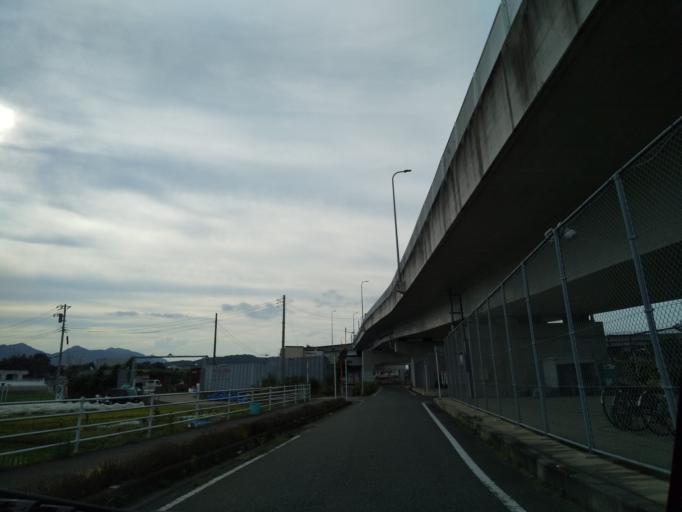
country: JP
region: Kanagawa
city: Zama
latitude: 35.4815
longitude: 139.3552
